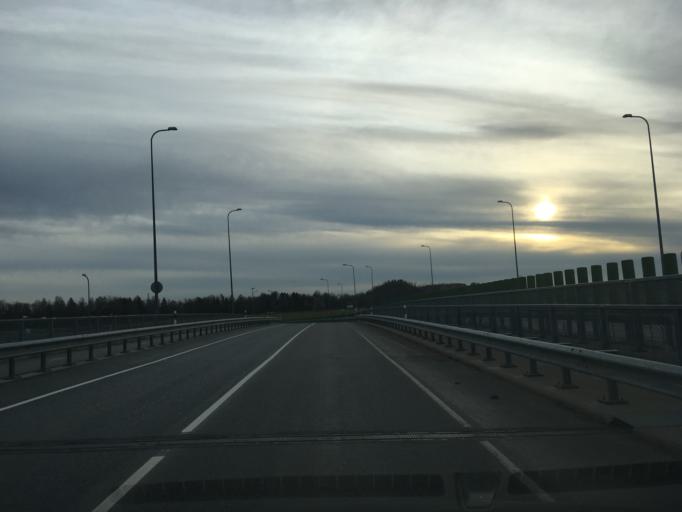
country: EE
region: Ida-Virumaa
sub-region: Johvi vald
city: Johvi
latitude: 59.3695
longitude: 27.3913
